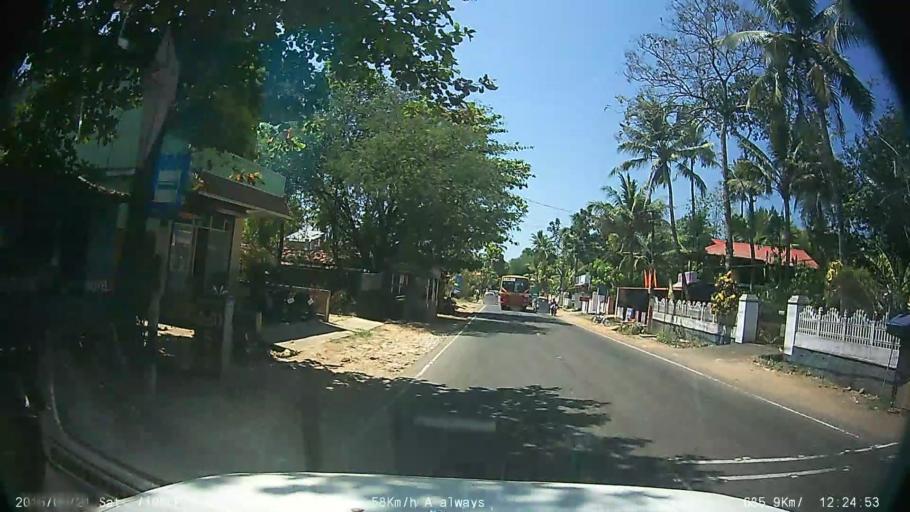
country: IN
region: Kerala
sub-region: Kottayam
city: Palackattumala
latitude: 9.6695
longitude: 76.5786
